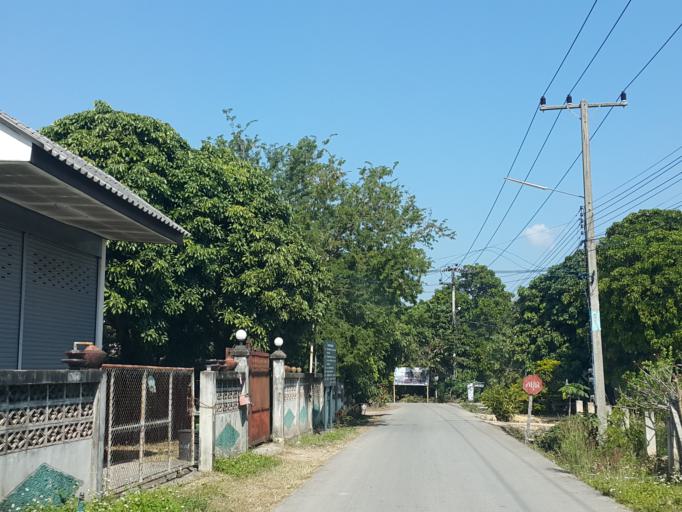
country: TH
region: Chiang Mai
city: San Sai
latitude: 18.9610
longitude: 98.9882
